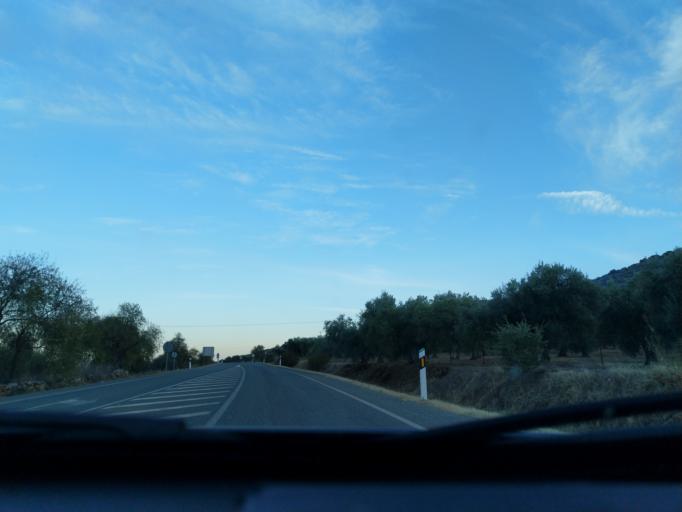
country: ES
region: Extremadura
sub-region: Provincia de Badajoz
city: Reina
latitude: 38.1887
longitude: -5.9434
